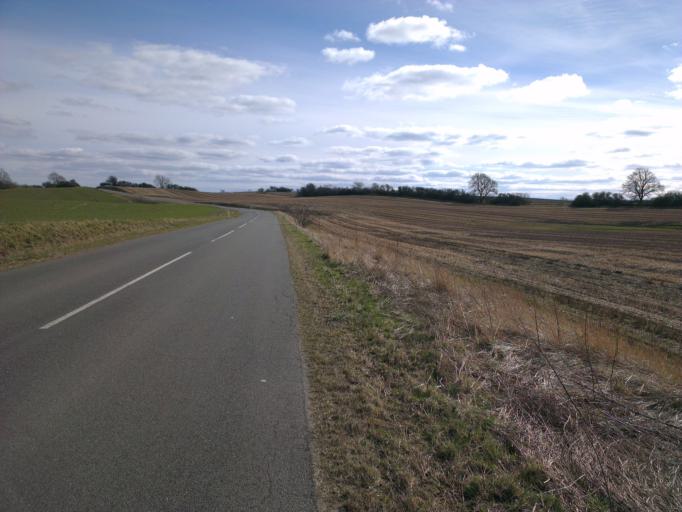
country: DK
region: Capital Region
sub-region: Frederikssund Kommune
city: Skibby
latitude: 55.7411
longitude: 12.0155
